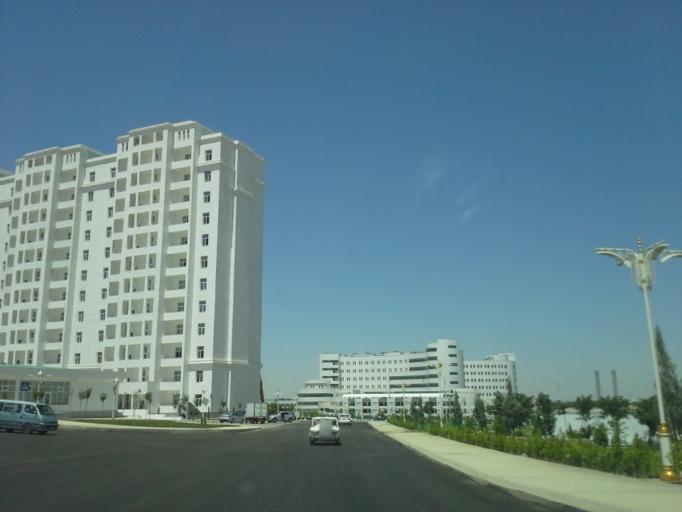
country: TM
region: Ahal
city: Ashgabat
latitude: 37.9377
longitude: 58.3623
